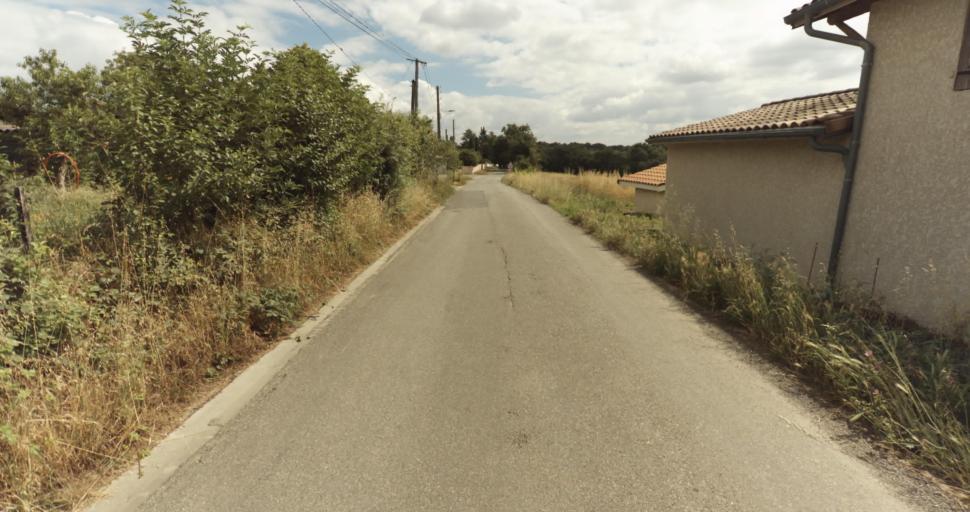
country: FR
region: Midi-Pyrenees
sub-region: Departement de la Haute-Garonne
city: Fontenilles
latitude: 43.5574
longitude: 1.2103
